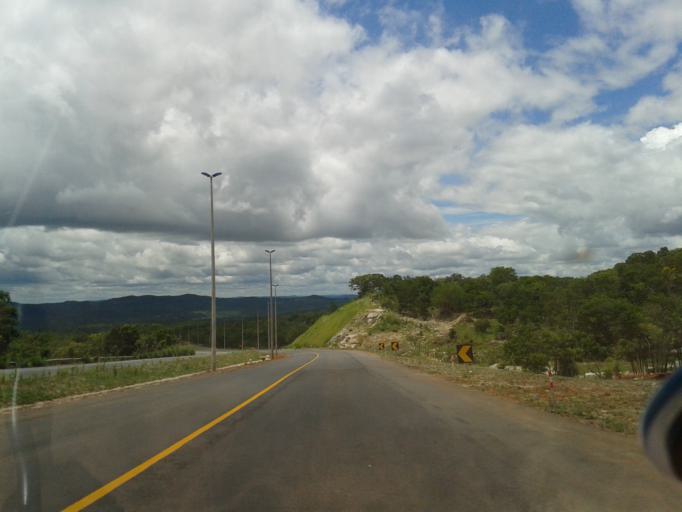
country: BR
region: Goias
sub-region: Goias
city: Goias
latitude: -15.9800
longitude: -50.0918
